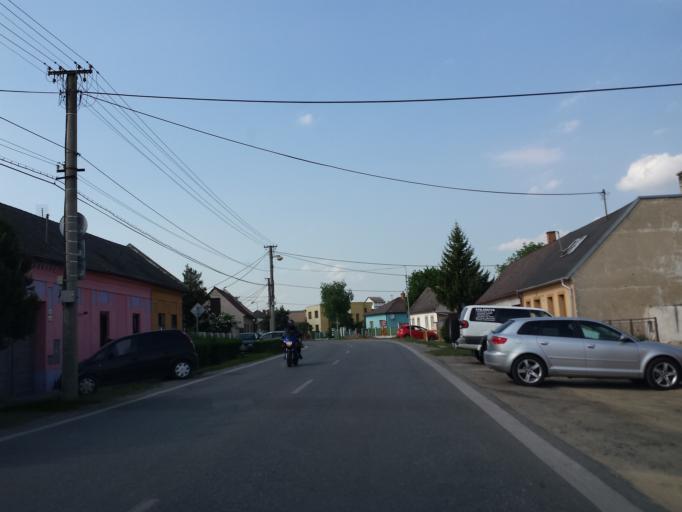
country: SK
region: Bratislavsky
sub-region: Okres Malacky
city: Malacky
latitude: 48.4275
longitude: 17.0210
